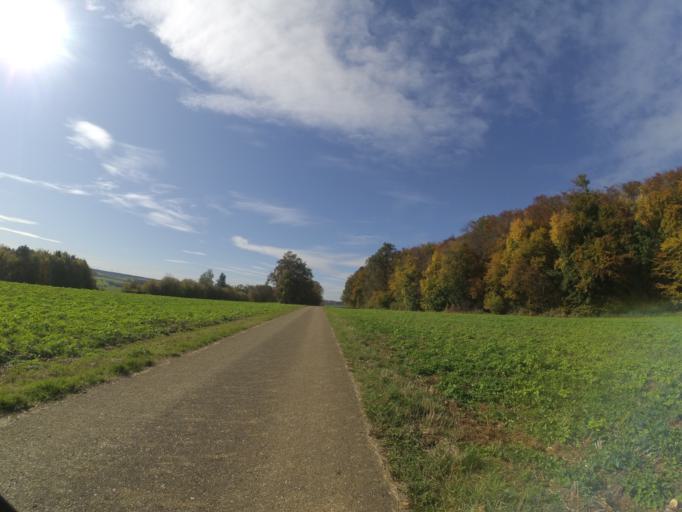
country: DE
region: Baden-Wuerttemberg
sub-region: Tuebingen Region
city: Lonsee
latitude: 48.5405
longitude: 9.9382
